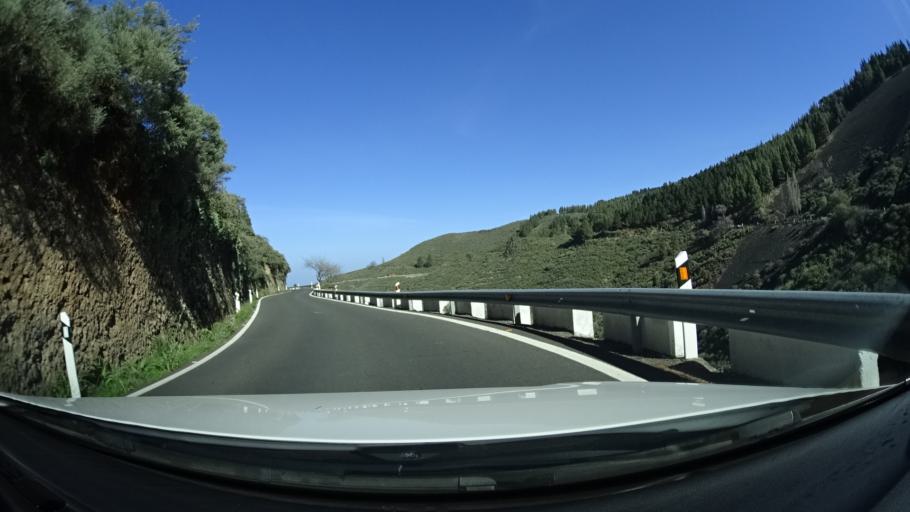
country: ES
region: Canary Islands
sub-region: Provincia de Las Palmas
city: Artenara
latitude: 28.0256
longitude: -15.6198
